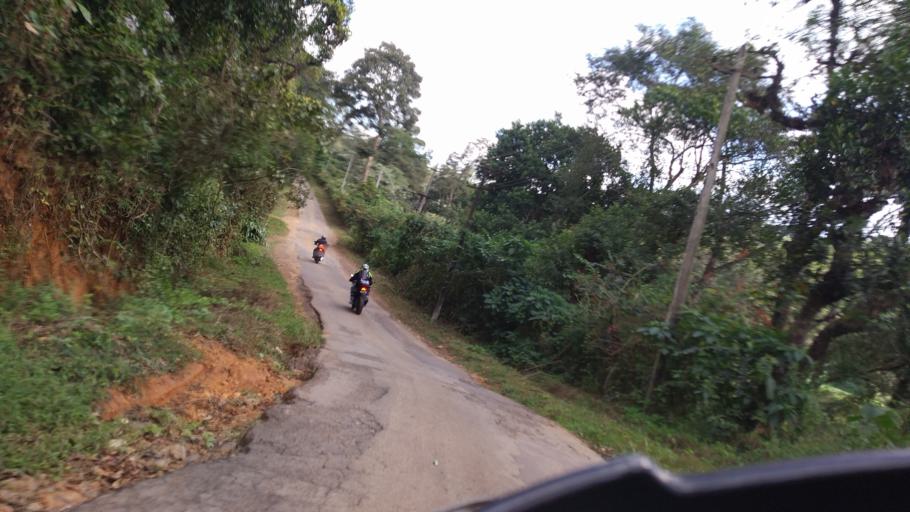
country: IN
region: Karnataka
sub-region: Kodagu
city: Ponnampet
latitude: 12.0344
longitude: 75.9109
